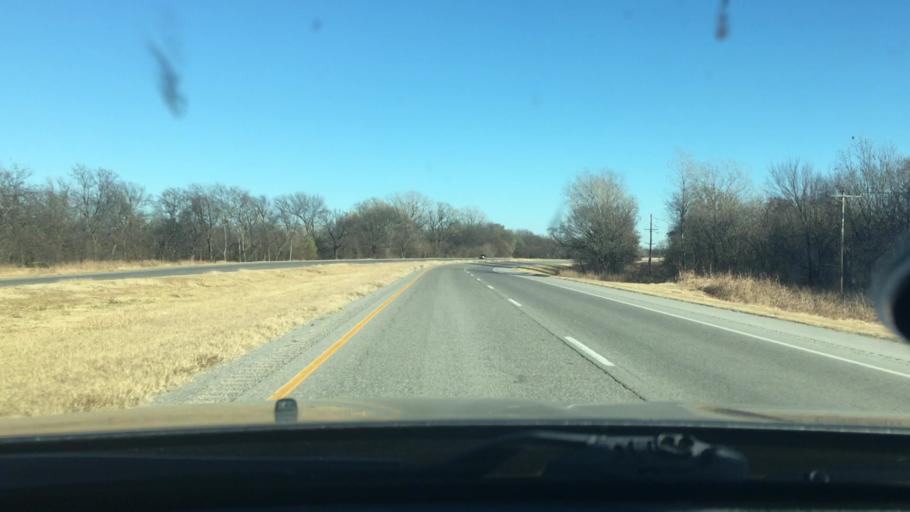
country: US
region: Oklahoma
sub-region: Murray County
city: Davis
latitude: 34.5064
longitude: -97.1520
